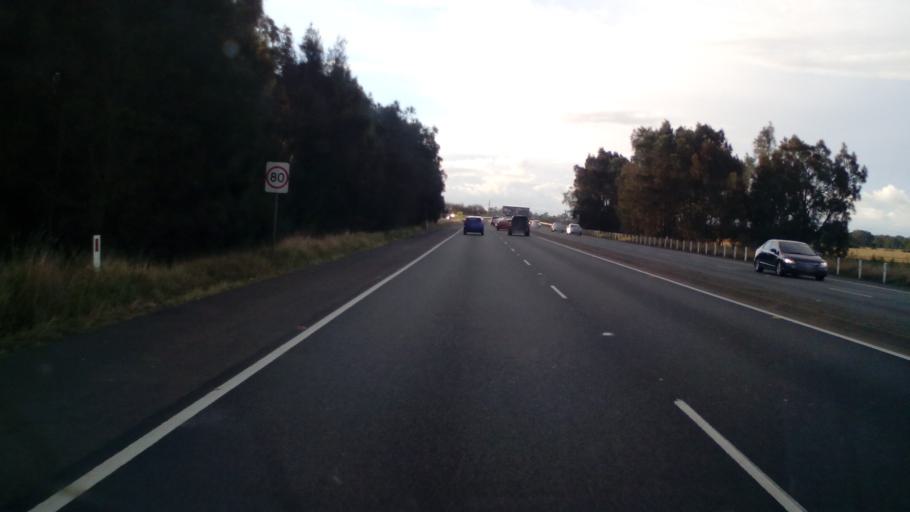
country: AU
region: New South Wales
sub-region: Newcastle
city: Beresfield
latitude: -32.8137
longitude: 151.6764
